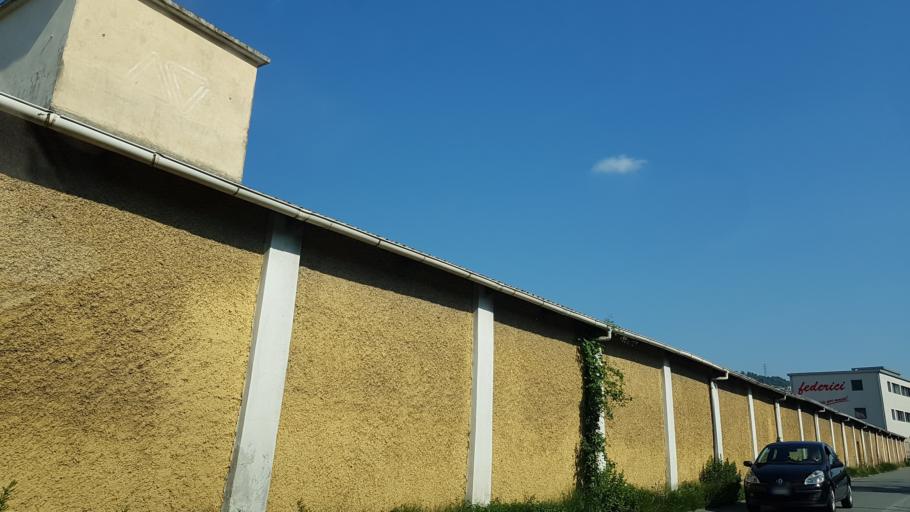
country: IT
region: Liguria
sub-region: Provincia di Genova
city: Manesseno
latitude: 44.4838
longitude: 8.9212
